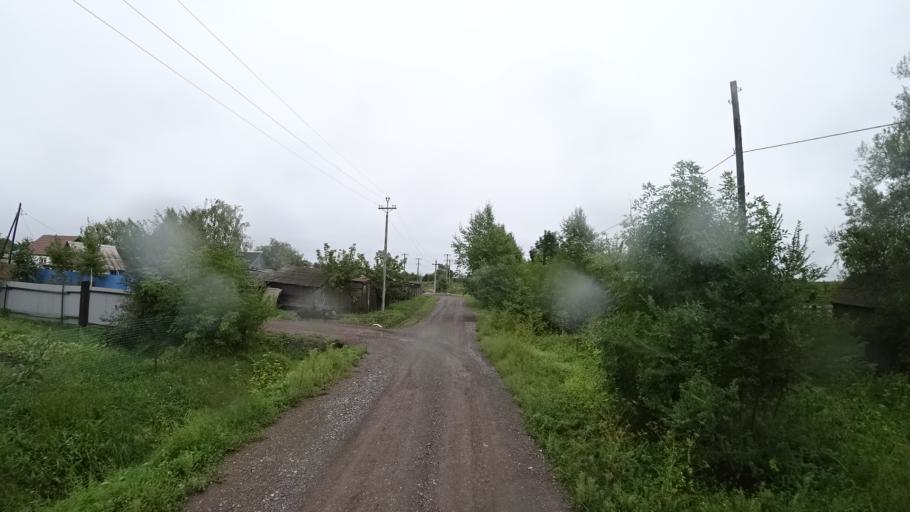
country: RU
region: Primorskiy
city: Monastyrishche
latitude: 44.1904
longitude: 132.4207
